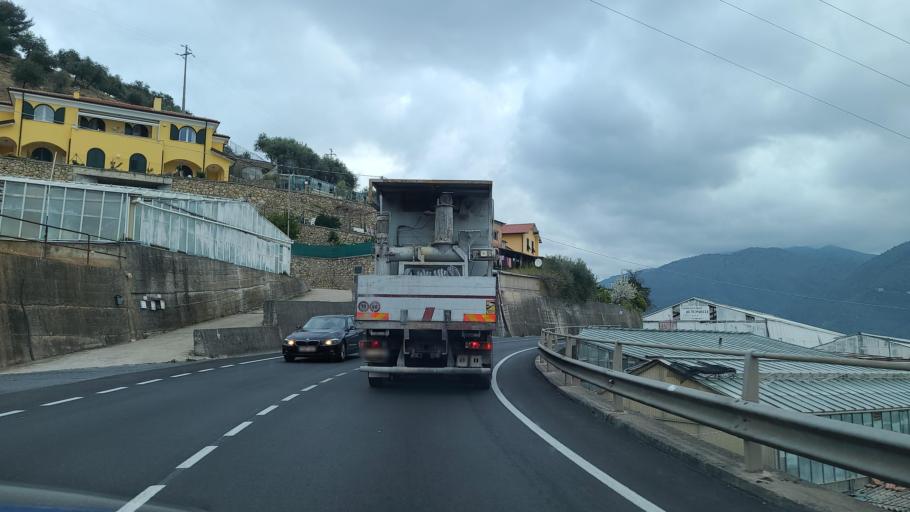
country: IT
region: Liguria
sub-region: Provincia di Imperia
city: Taggia
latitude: 43.8477
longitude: 7.8409
